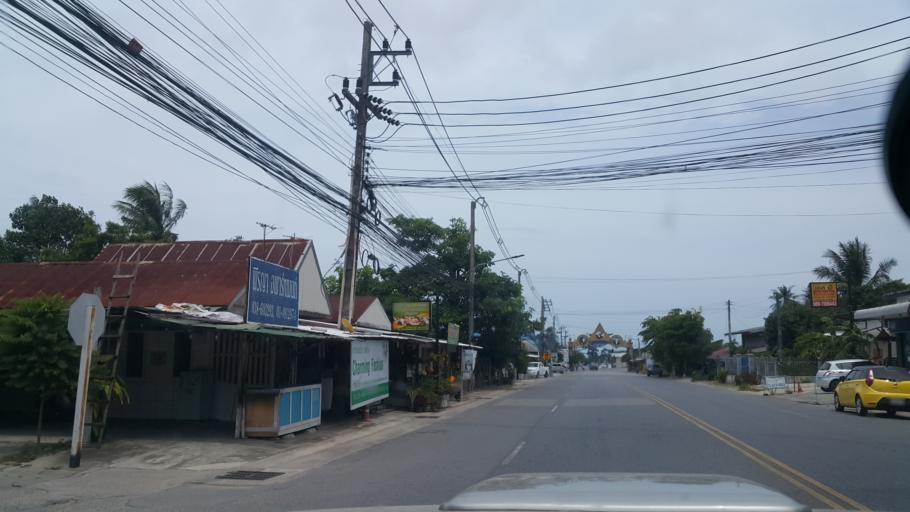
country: TH
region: Rayong
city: Ban Chang
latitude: 12.7139
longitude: 101.0492
